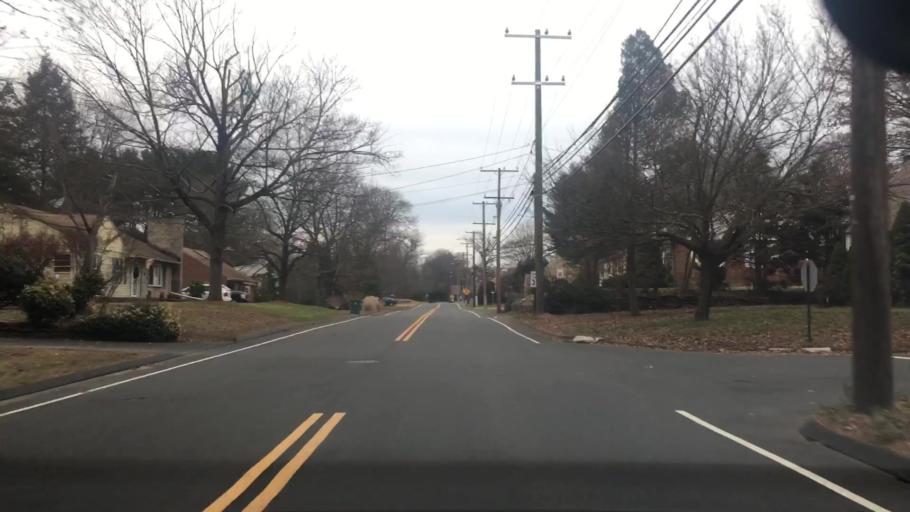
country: US
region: Connecticut
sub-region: Hartford County
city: Plainville
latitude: 41.6655
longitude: -72.9022
